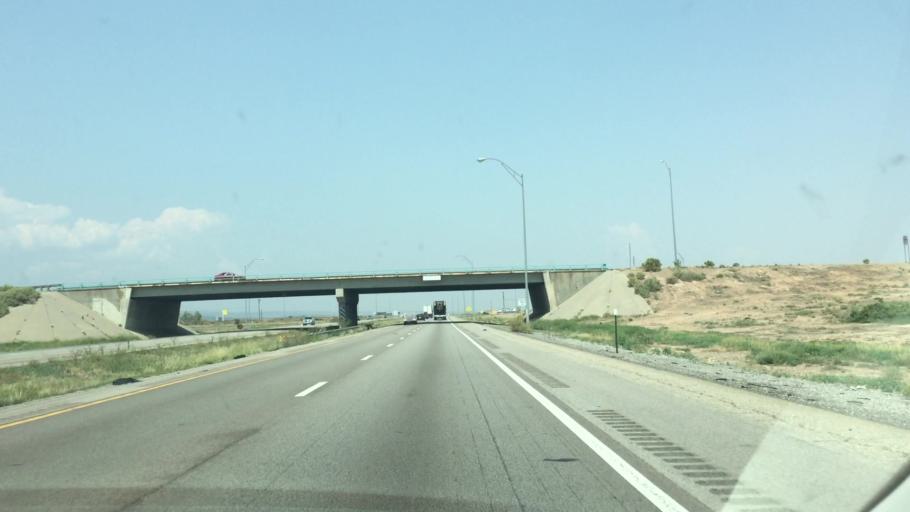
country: US
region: New Mexico
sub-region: Cibola County
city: Grants
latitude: 35.1234
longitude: -107.8284
